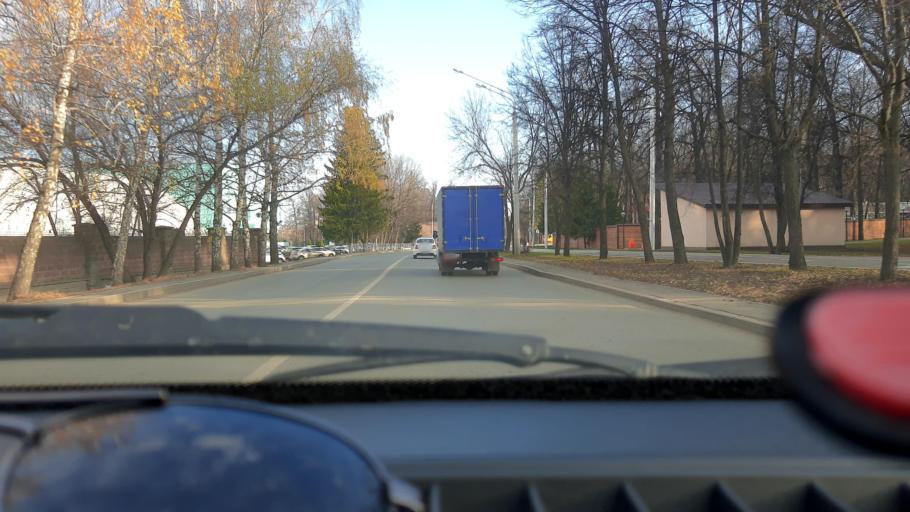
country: RU
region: Bashkortostan
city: Ufa
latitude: 54.7722
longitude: 56.0164
